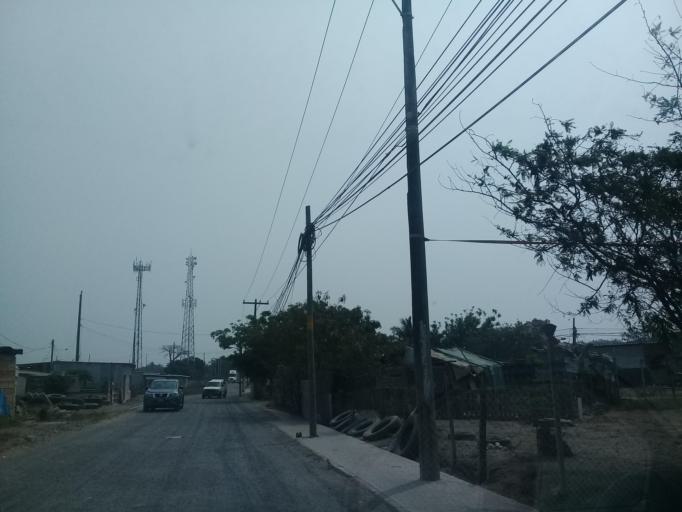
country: MX
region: Veracruz
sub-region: Veracruz
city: Fraccionamiento Costa Dorada
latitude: 19.2107
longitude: -96.2204
